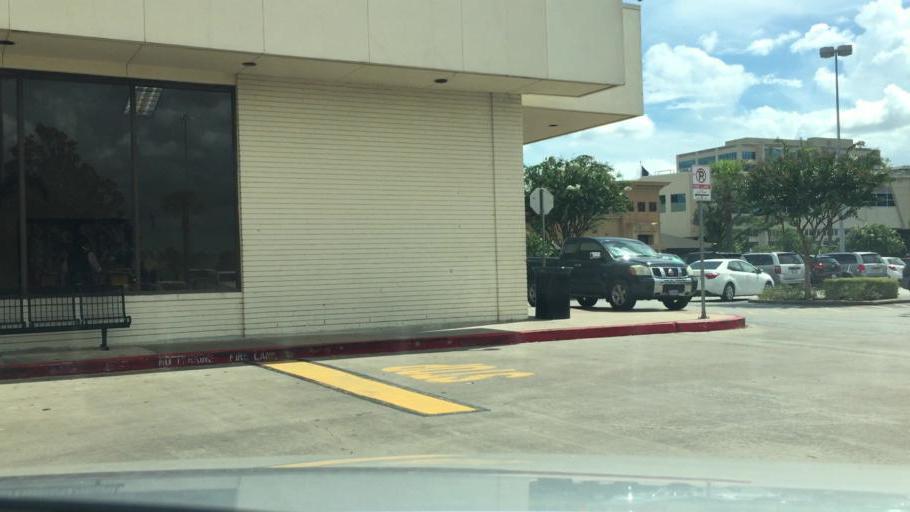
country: US
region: Texas
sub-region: Harris County
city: Bunker Hill Village
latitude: 29.7826
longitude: -95.5421
